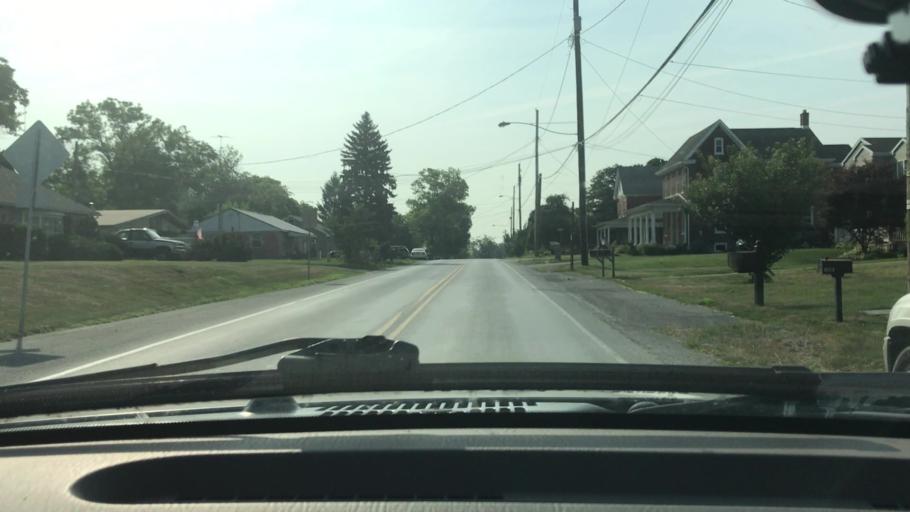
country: US
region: Pennsylvania
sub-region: Lancaster County
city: Rheems
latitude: 40.1305
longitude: -76.5699
